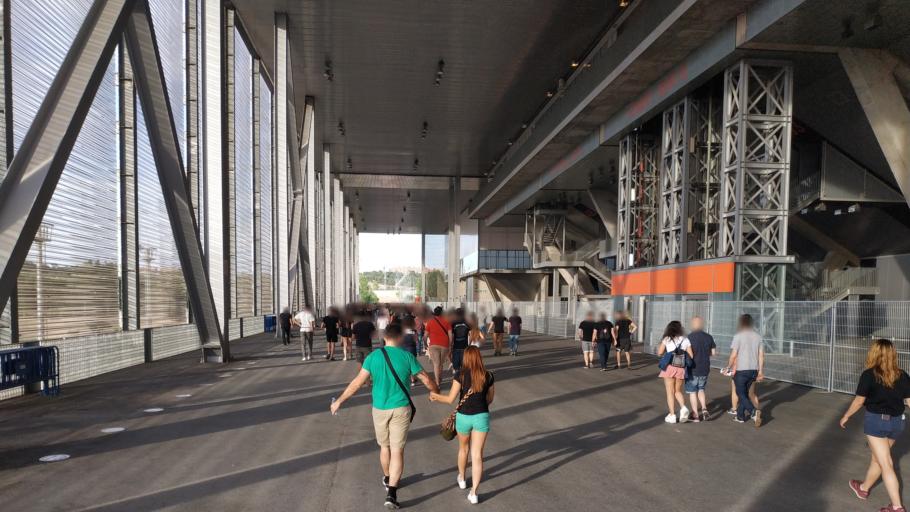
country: ES
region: Madrid
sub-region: Provincia de Madrid
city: Villaverde
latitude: 40.3692
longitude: -3.6854
